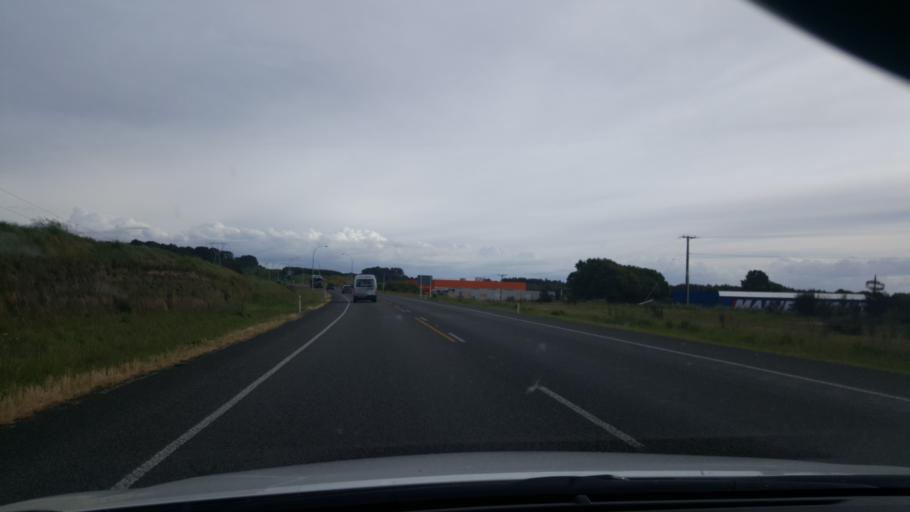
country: NZ
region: Waikato
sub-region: Taupo District
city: Taupo
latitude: -38.6996
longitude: 176.1121
